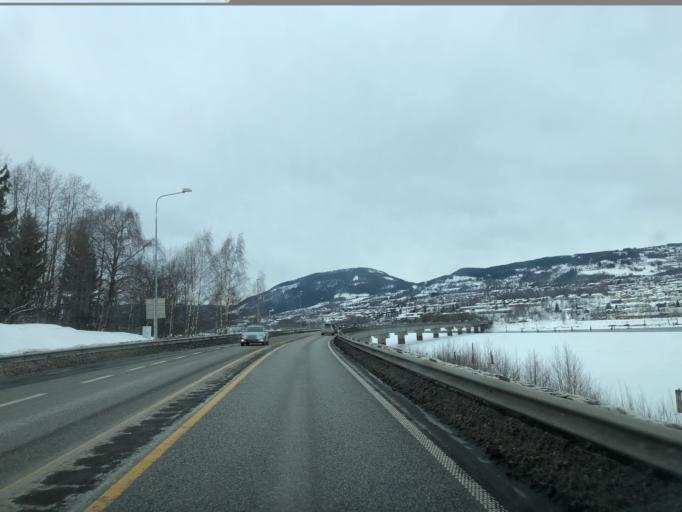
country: NO
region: Oppland
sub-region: Lillehammer
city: Lillehammer
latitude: 61.1081
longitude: 10.4425
